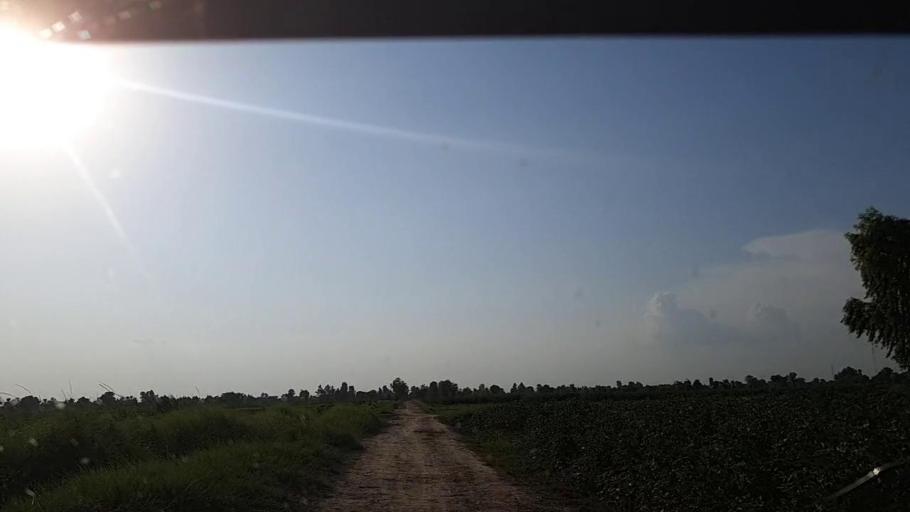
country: PK
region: Sindh
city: Pano Aqil
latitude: 27.9059
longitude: 69.2066
